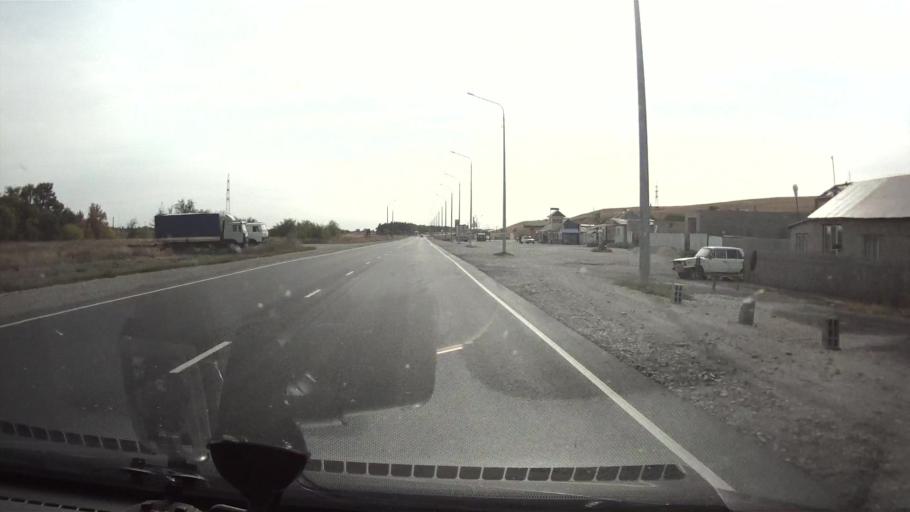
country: RU
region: Saratov
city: Sinodskoye
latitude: 52.0840
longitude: 46.7997
